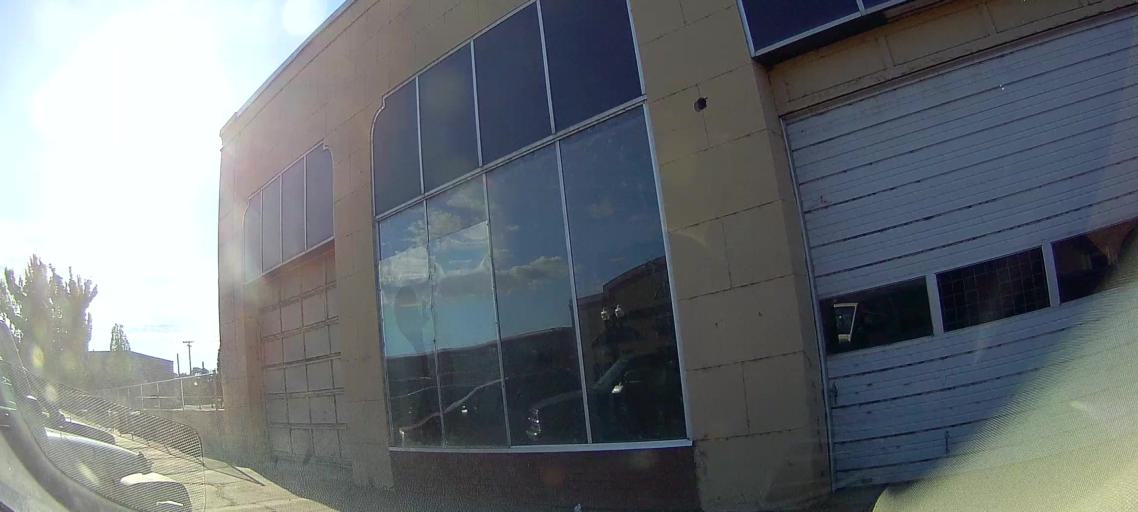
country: US
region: Oregon
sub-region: Klamath County
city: Klamath Falls
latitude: 42.2283
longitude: -121.7762
